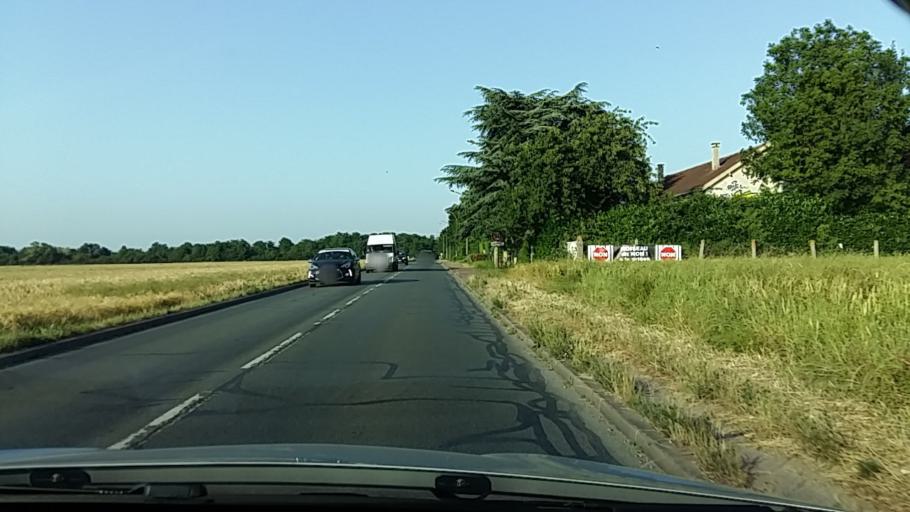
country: FR
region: Ile-de-France
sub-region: Departement du Val-de-Marne
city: Noiseau
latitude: 48.7789
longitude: 2.5564
